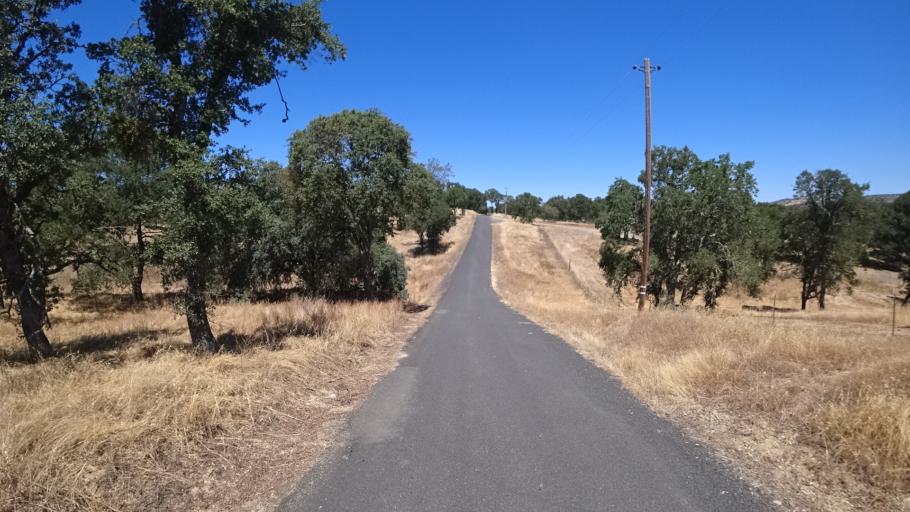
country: US
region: California
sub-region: Calaveras County
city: Copperopolis
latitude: 37.9652
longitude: -120.6738
